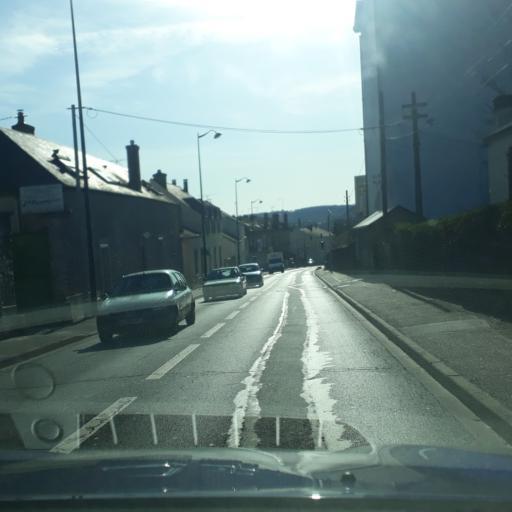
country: FR
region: Ile-de-France
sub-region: Departement de l'Essonne
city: Etampes
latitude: 48.4394
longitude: 2.1595
